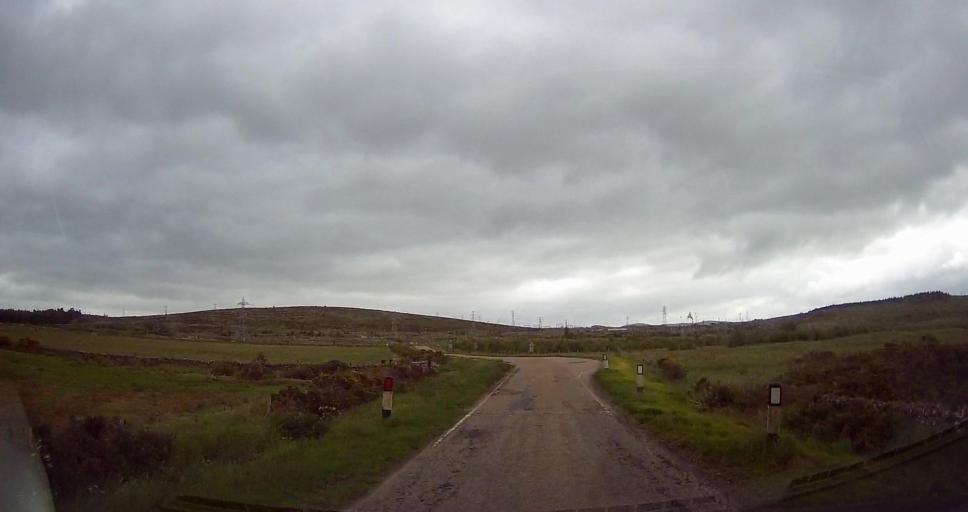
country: GB
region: Scotland
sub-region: Highland
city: Alness
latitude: 58.0561
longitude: -4.4256
